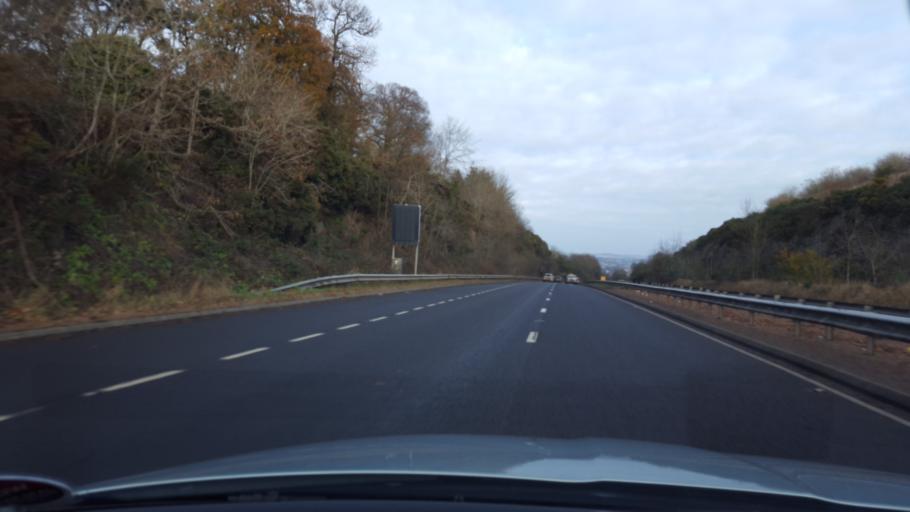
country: GB
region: Scotland
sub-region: Fife
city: Newport-On-Tay
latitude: 56.4403
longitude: -2.9331
